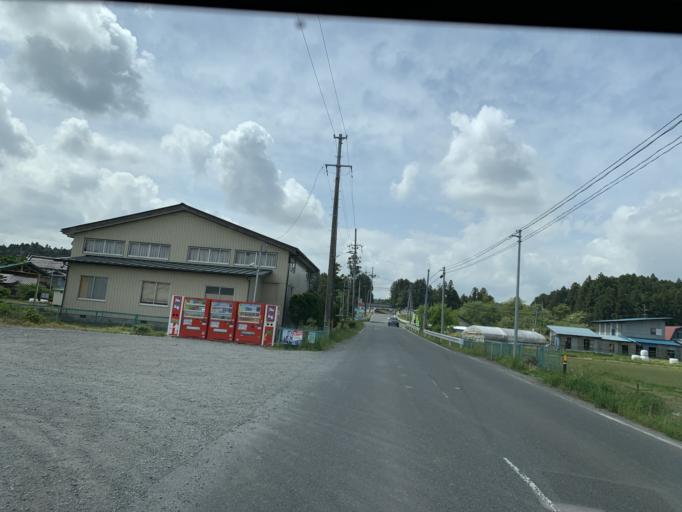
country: JP
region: Iwate
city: Ichinoseki
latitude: 38.7925
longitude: 141.0039
